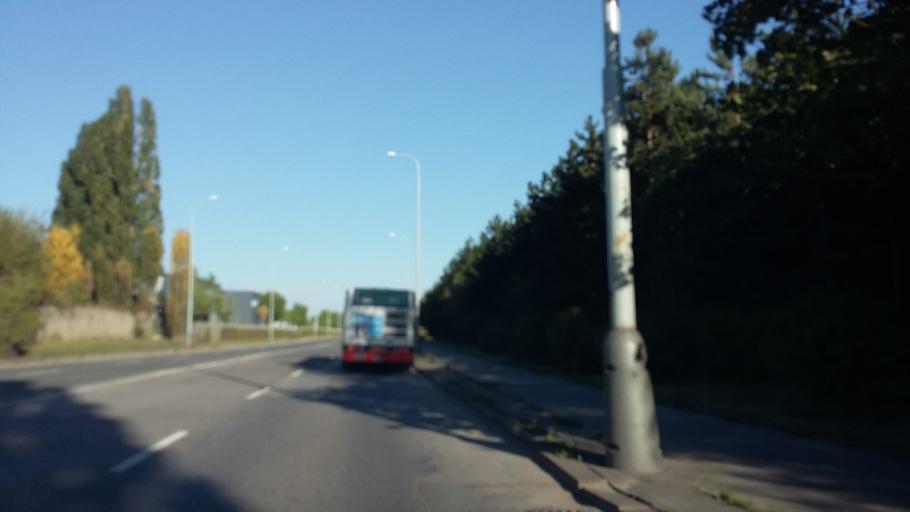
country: CZ
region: Praha
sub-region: Praha 18
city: Letnany
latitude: 50.1427
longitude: 14.5091
